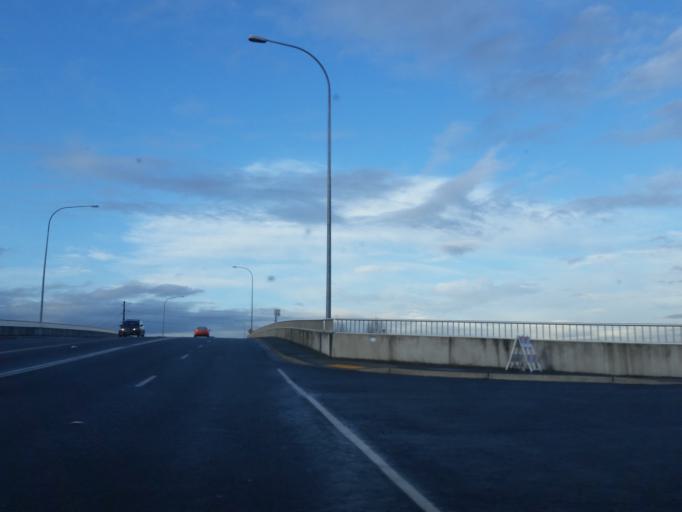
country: US
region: Washington
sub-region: Pierce County
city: Sumner
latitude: 47.1881
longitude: -122.2567
